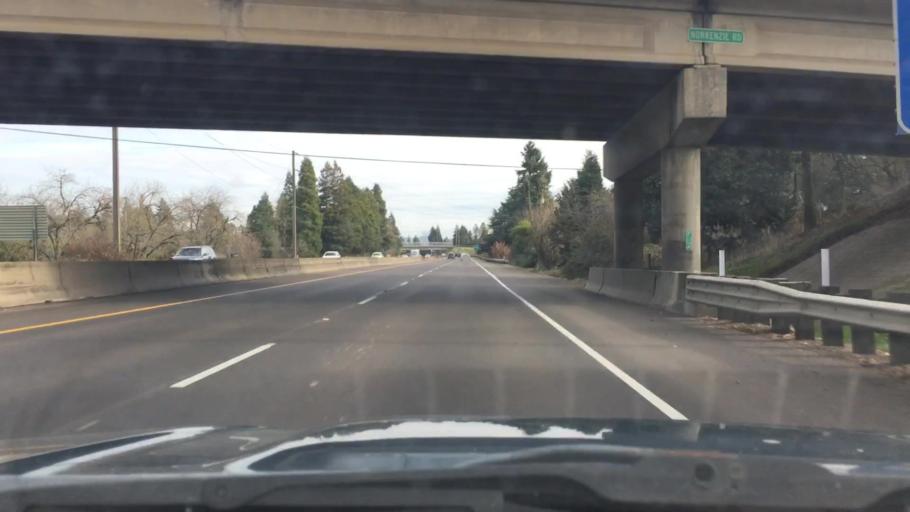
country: US
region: Oregon
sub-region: Lane County
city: Eugene
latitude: 44.0890
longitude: -123.0884
